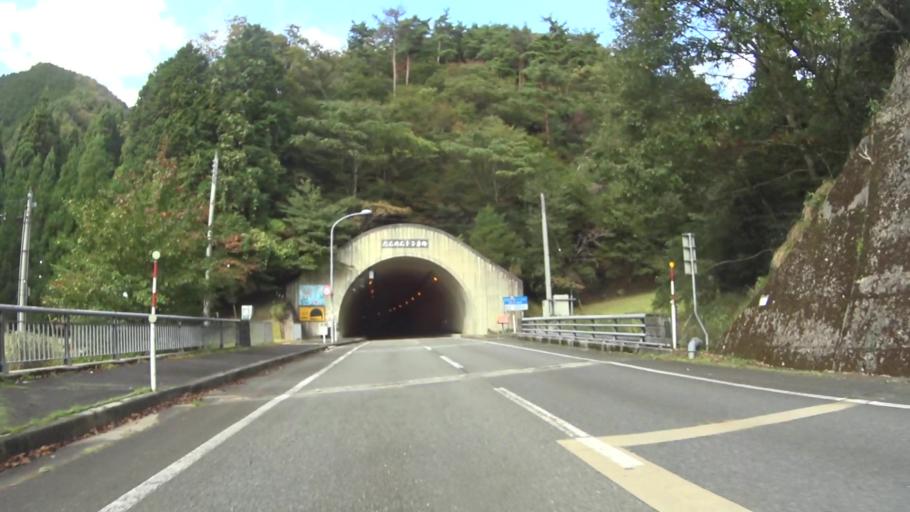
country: JP
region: Hyogo
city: Toyooka
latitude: 35.5237
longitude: 134.9873
